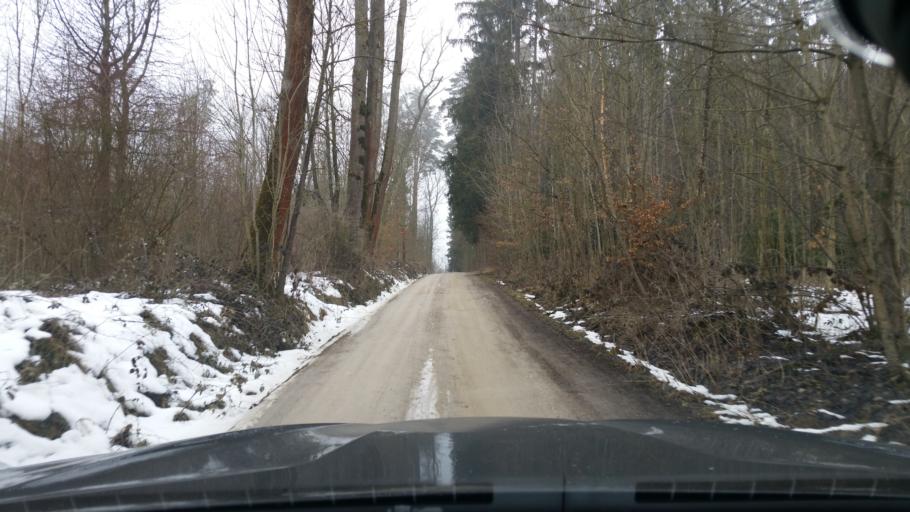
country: DE
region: Bavaria
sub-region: Lower Bavaria
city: Ergolding
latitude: 48.5778
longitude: 12.1258
